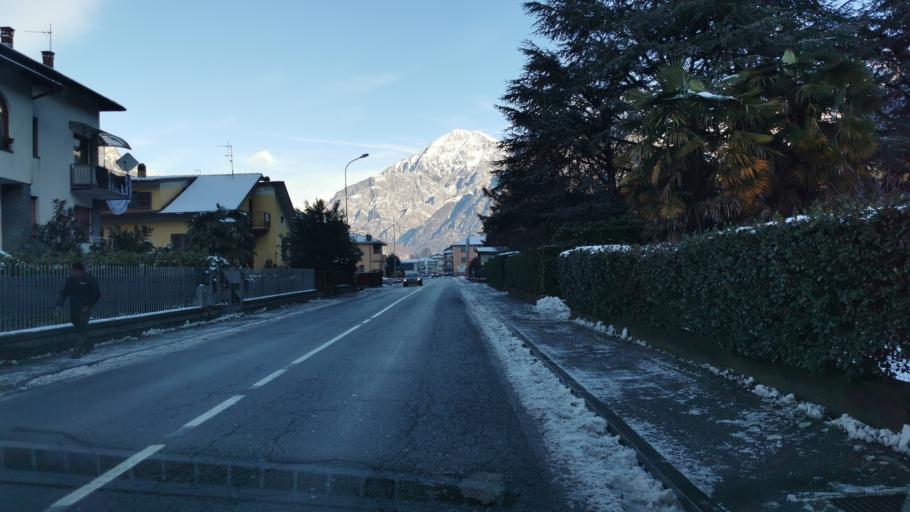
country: IT
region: Lombardy
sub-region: Provincia di Sondrio
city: Dubino
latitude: 46.1688
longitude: 9.4323
